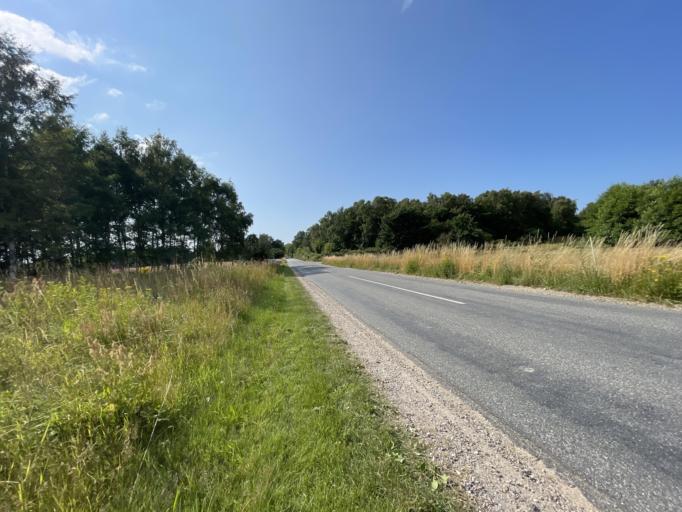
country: DK
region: Capital Region
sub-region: Gribskov Kommune
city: Helsinge
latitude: 56.0897
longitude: 12.1784
